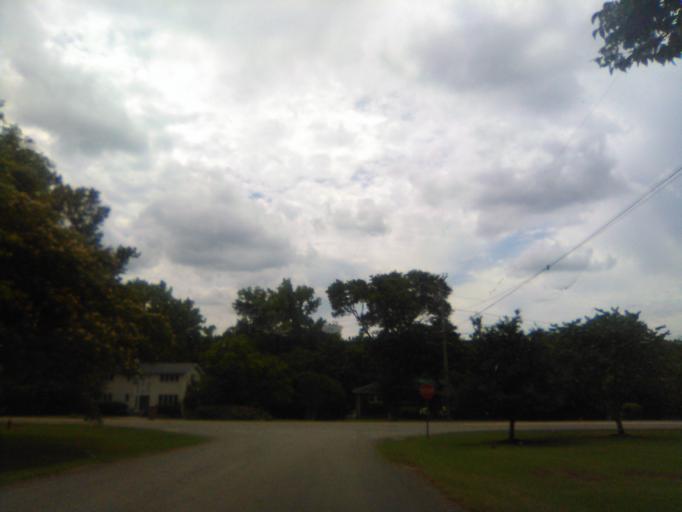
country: US
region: Tennessee
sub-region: Davidson County
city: Belle Meade
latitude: 36.1296
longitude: -86.8937
